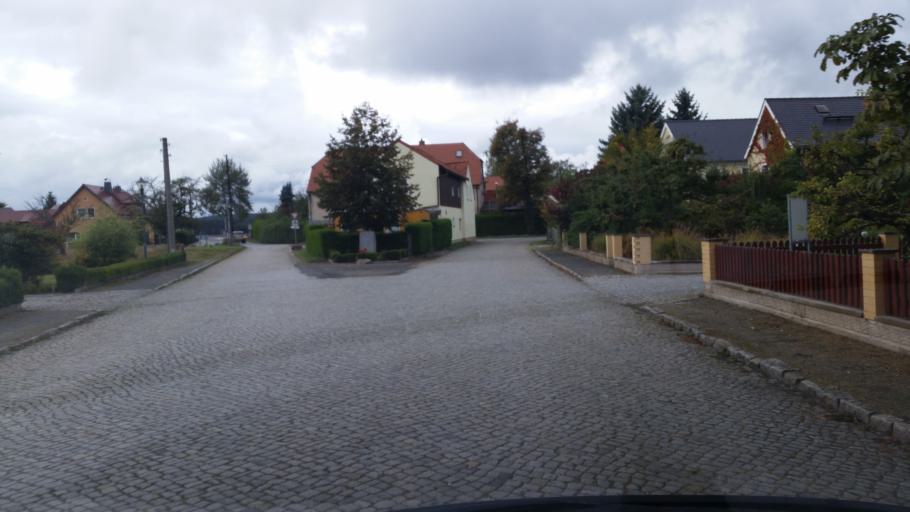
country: DE
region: Saxony
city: Ossling
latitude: 51.3136
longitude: 14.1388
